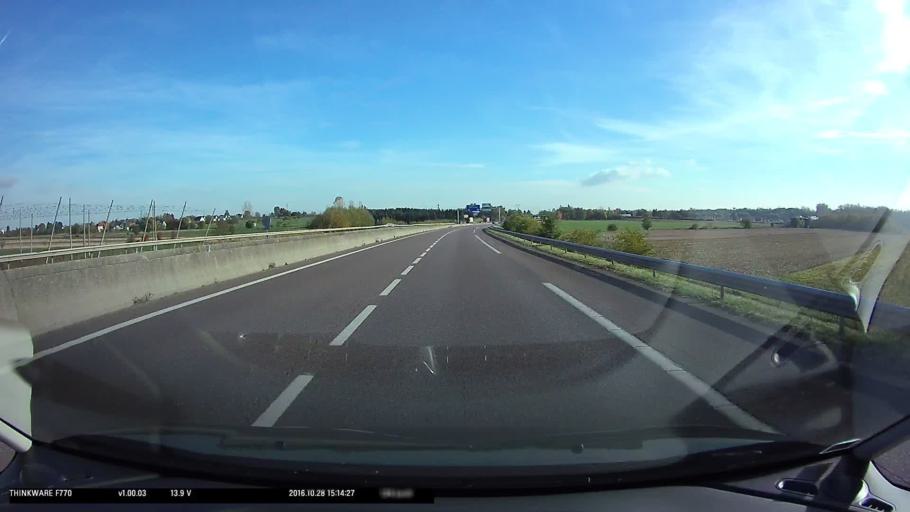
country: FR
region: Alsace
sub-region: Departement du Bas-Rhin
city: Mommenheim
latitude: 48.7537
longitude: 7.6773
